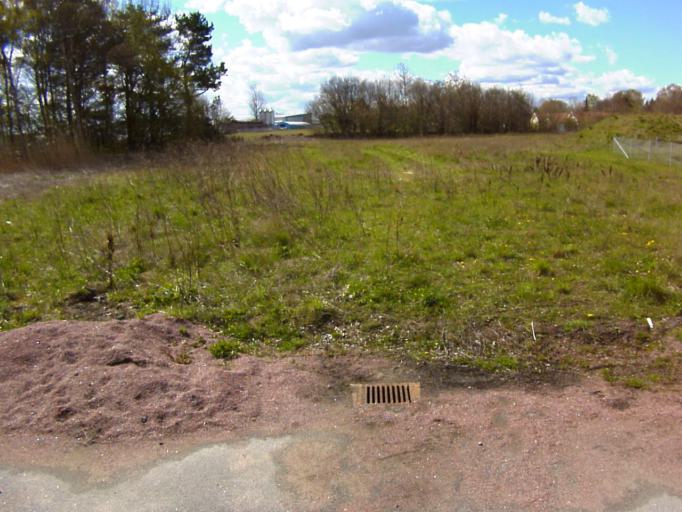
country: SE
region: Skane
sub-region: Kristianstads Kommun
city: Norra Asum
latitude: 56.0073
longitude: 14.1011
